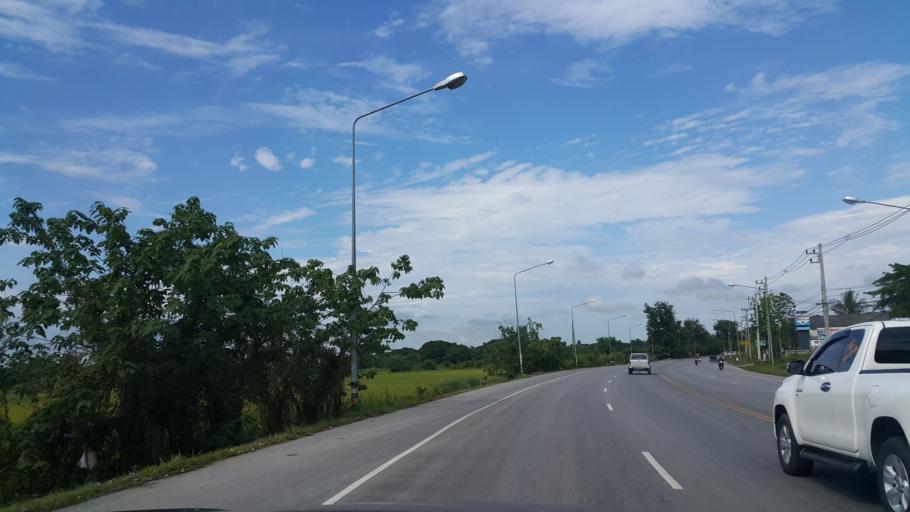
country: TH
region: Chiang Rai
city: Chiang Rai
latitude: 19.9126
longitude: 99.8654
